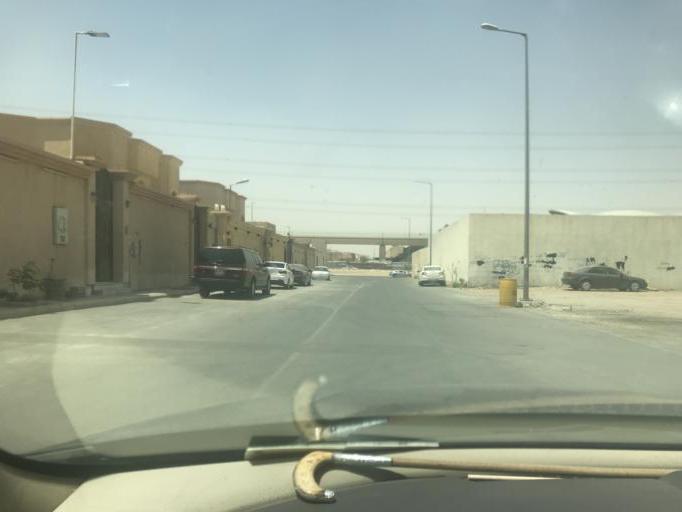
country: SA
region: Ar Riyad
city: Riyadh
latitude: 24.7991
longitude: 46.6960
